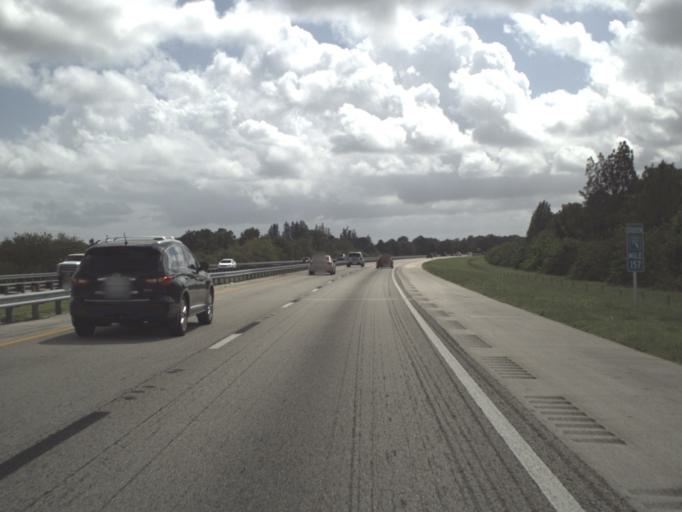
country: US
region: Florida
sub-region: Saint Lucie County
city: Lakewood Park
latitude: 27.4599
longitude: -80.4328
